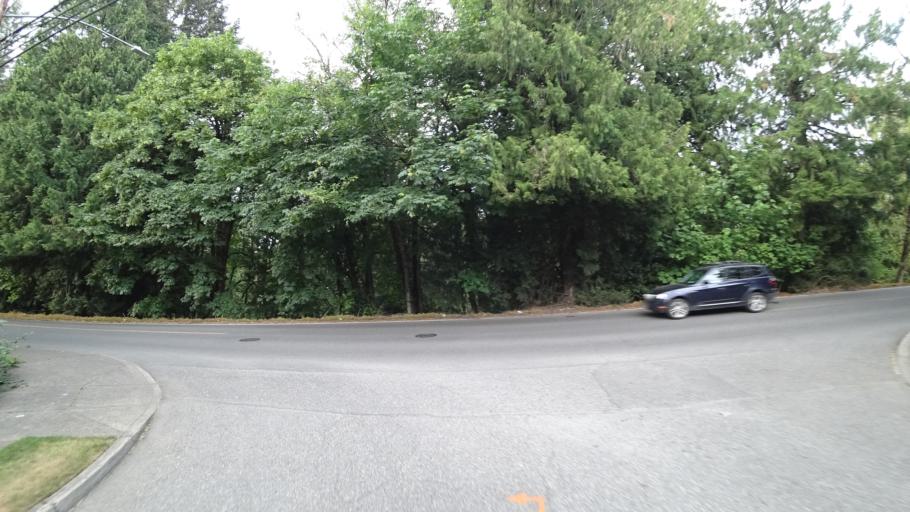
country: US
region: Oregon
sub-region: Clackamas County
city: Happy Valley
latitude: 45.4732
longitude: -122.4975
